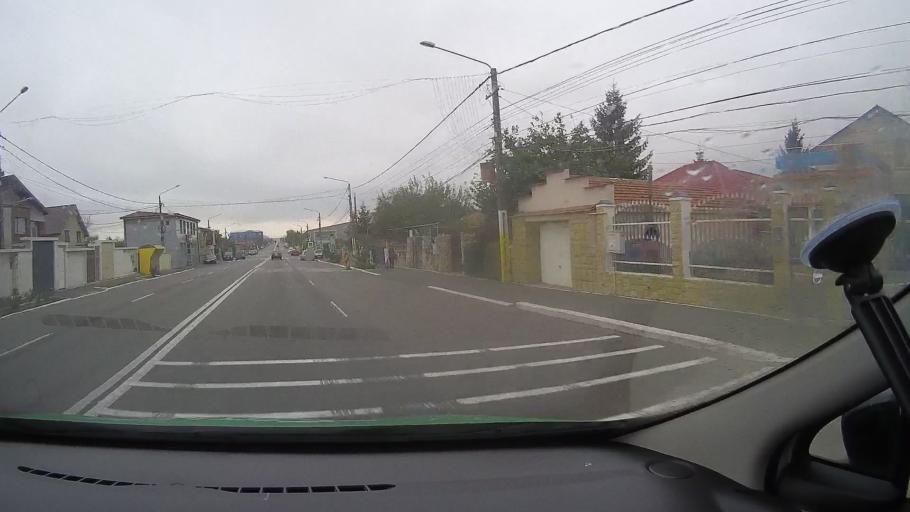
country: RO
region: Constanta
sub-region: Comuna Valu lui Traian
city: Valu lui Traian
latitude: 44.1652
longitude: 28.4691
